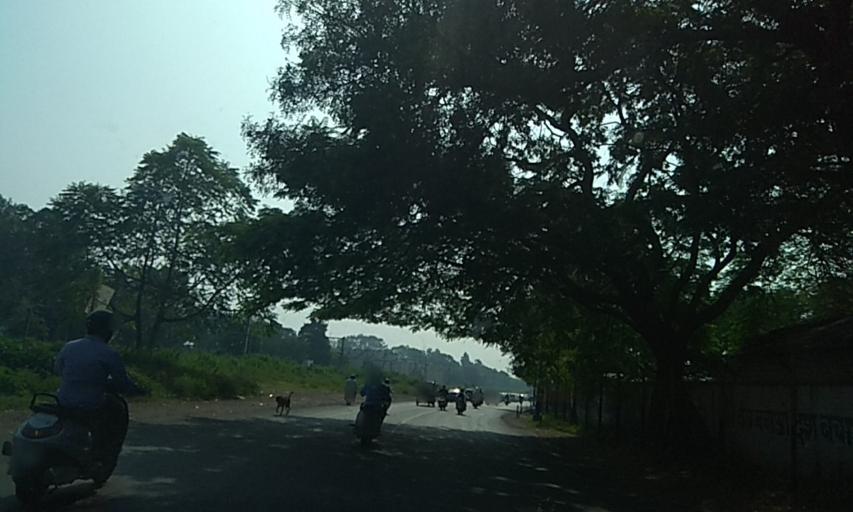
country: IN
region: Maharashtra
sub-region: Pune Division
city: Khadki
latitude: 18.5596
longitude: 73.8429
